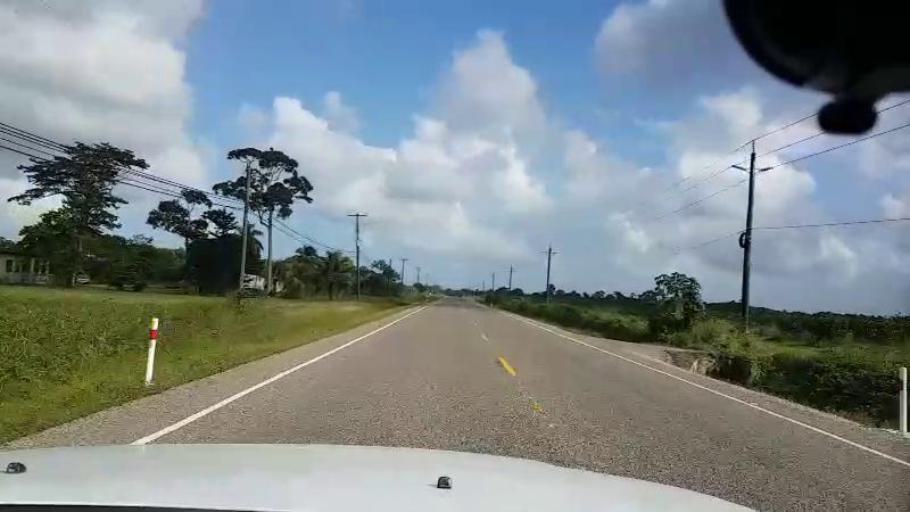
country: BZ
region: Stann Creek
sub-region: Dangriga
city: Dangriga
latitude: 16.9972
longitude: -88.3441
